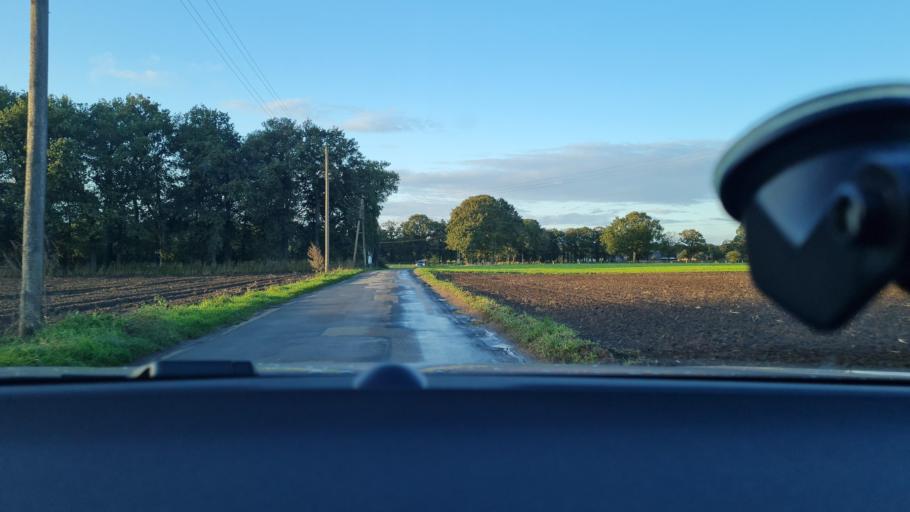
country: DE
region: North Rhine-Westphalia
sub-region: Regierungsbezirk Dusseldorf
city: Dinslaken
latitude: 51.5969
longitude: 6.7341
